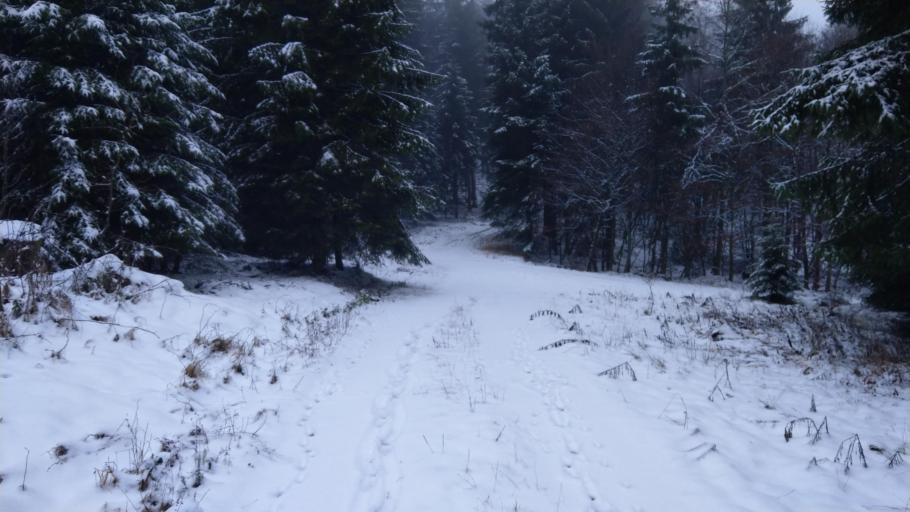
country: DE
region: North Rhine-Westphalia
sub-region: Regierungsbezirk Arnsberg
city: Erndtebruck
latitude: 50.9820
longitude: 8.1893
